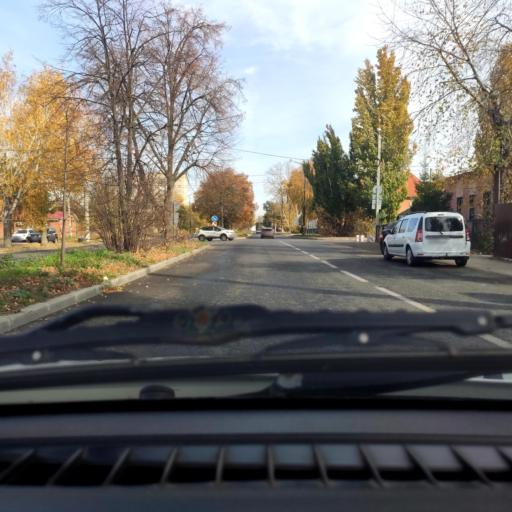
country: RU
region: Samara
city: Tol'yatti
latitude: 53.5160
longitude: 49.3997
